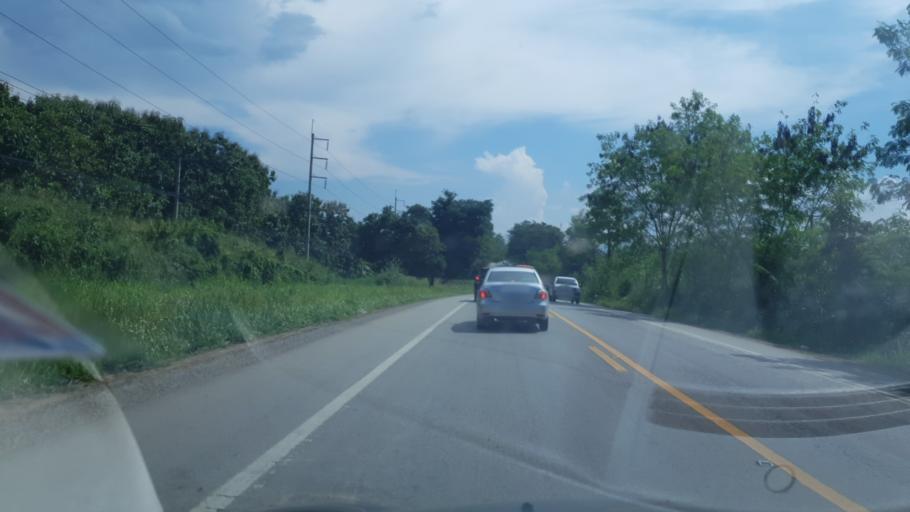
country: TH
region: Chiang Rai
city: Wiang Pa Pao
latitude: 19.4157
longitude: 99.5000
